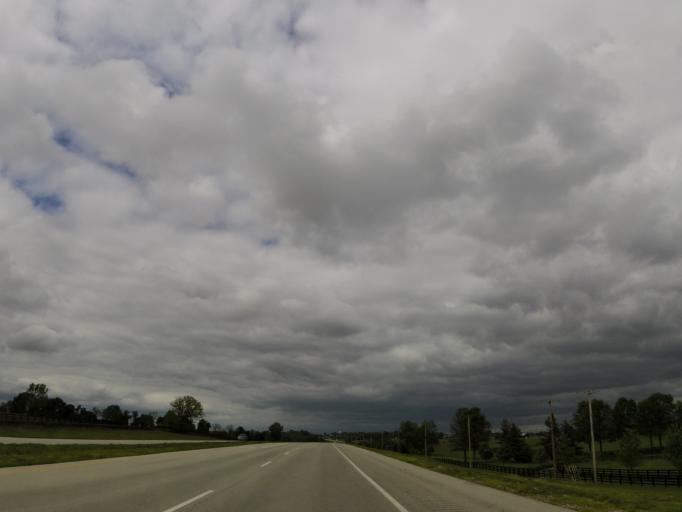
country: US
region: Kentucky
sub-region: Scott County
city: Georgetown
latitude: 38.1815
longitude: -84.5936
